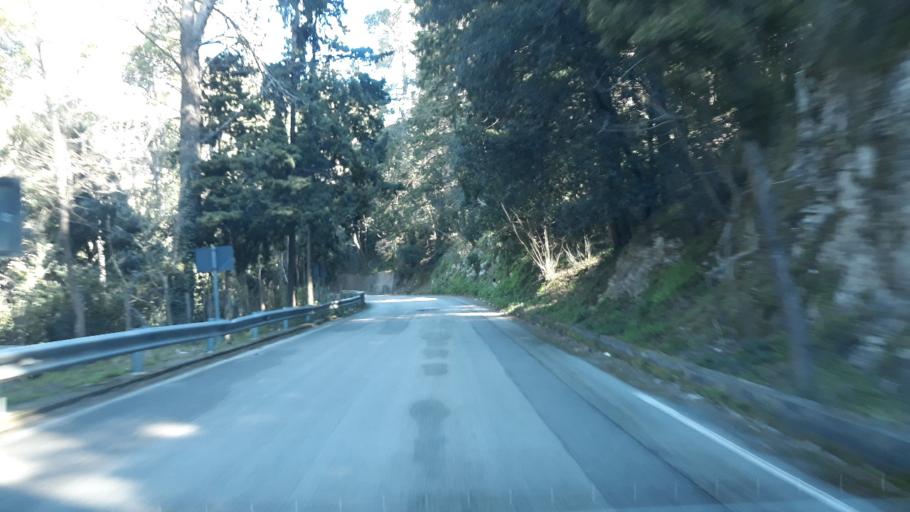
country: IT
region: Sicily
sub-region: Palermo
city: Piano dei Geli
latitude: 38.0904
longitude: 13.2530
